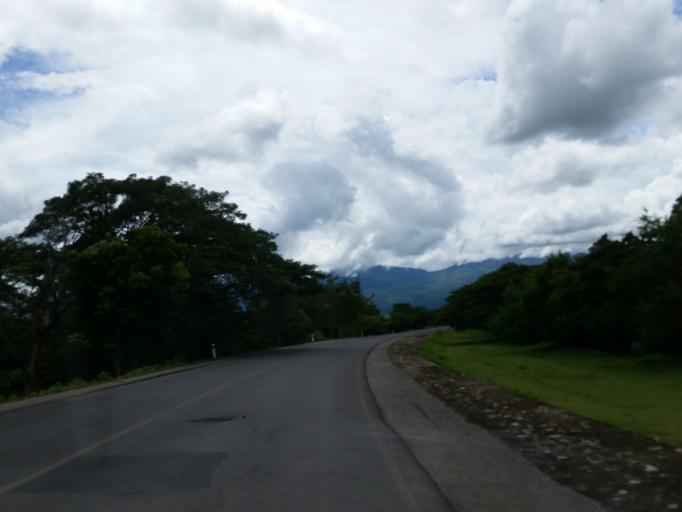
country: NI
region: Chinandega
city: Somotillo
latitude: 12.8066
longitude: -86.9033
